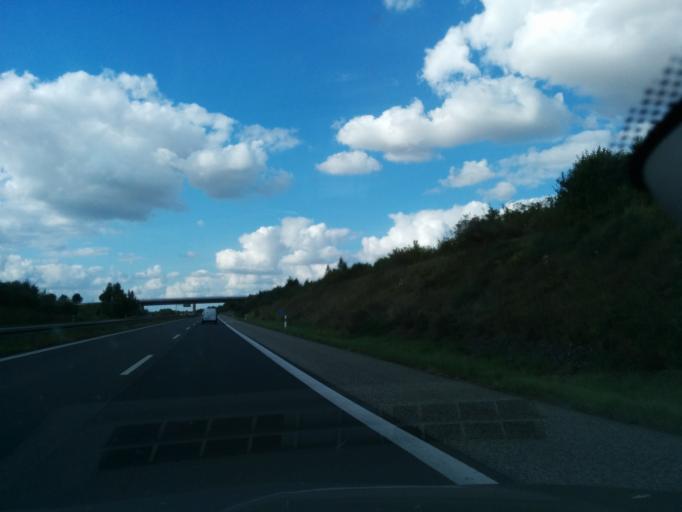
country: DE
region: Brandenburg
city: Gramzow
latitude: 53.2616
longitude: 13.9990
